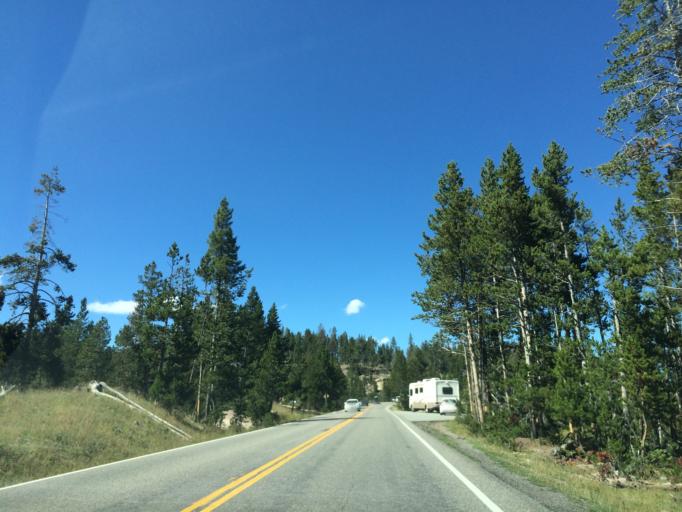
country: US
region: Montana
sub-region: Gallatin County
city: West Yellowstone
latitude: 44.6239
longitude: -110.4317
